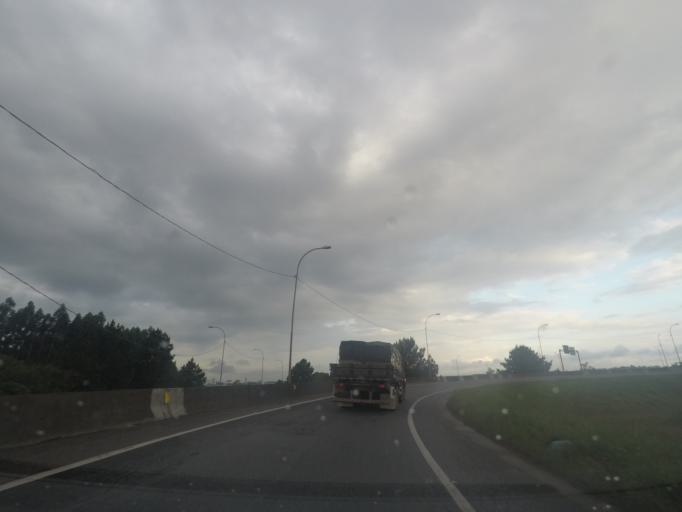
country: BR
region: Parana
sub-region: Sao Jose Dos Pinhais
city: Sao Jose dos Pinhais
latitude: -25.5675
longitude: -49.1807
